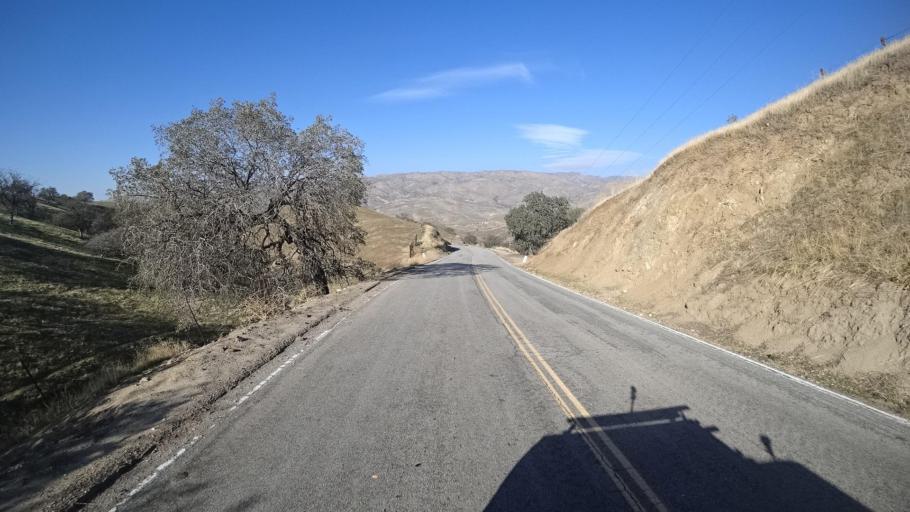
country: US
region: California
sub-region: Kern County
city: Bear Valley Springs
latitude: 35.2778
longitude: -118.6242
